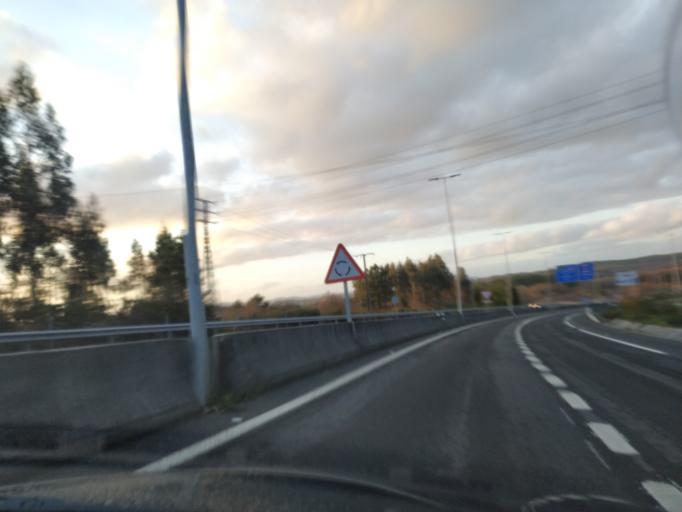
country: ES
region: Galicia
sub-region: Provincia da Coruna
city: Oroso
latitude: 42.9075
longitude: -8.4315
